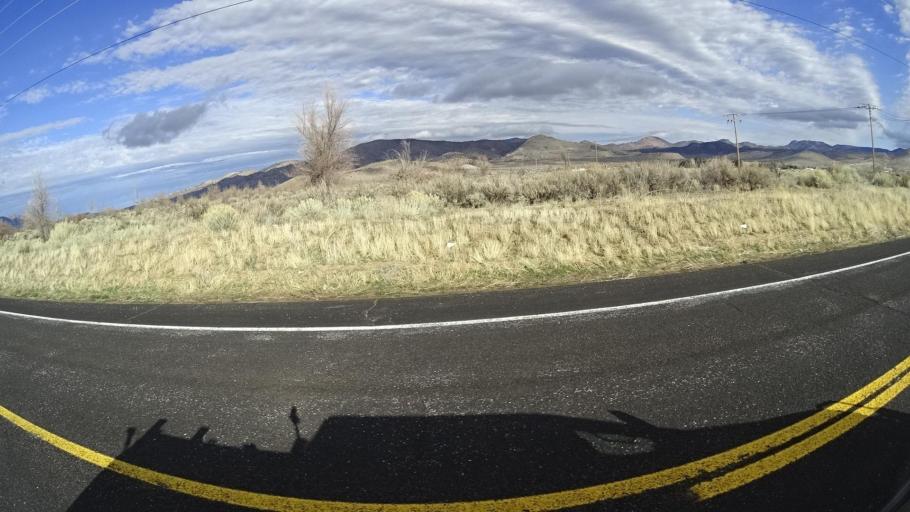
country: US
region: California
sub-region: Kern County
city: Tehachapi
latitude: 35.1097
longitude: -118.4062
